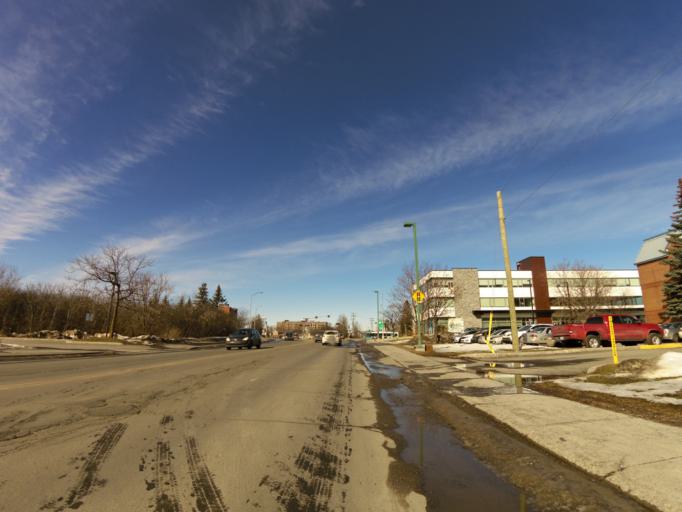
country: CA
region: Quebec
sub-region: Outaouais
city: Gatineau
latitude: 45.4452
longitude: -75.7508
